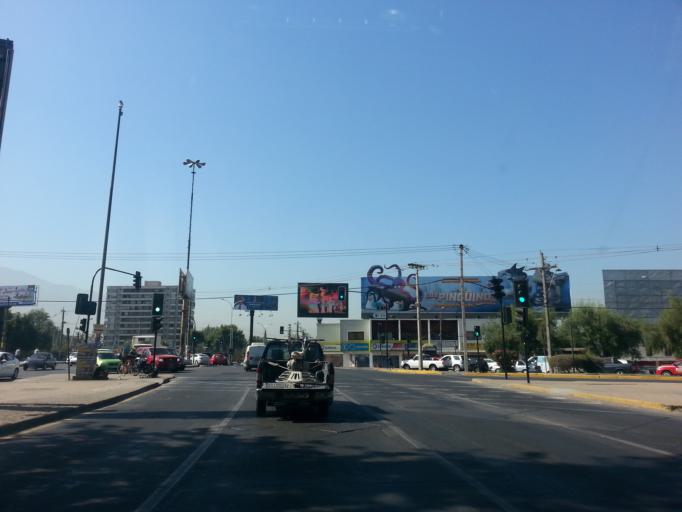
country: CL
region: Santiago Metropolitan
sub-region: Provincia de Santiago
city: Villa Presidente Frei, Nunoa, Santiago, Chile
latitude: -33.4375
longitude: -70.5738
